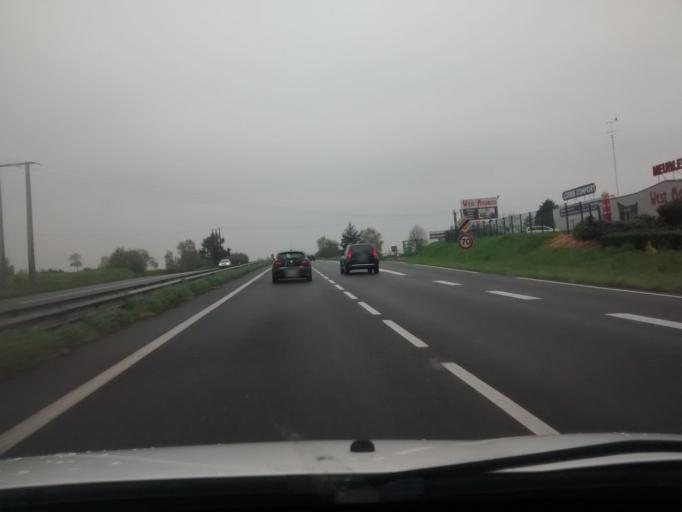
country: FR
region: Brittany
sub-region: Departement des Cotes-d'Armor
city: Lamballe
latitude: 48.4659
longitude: -2.5464
